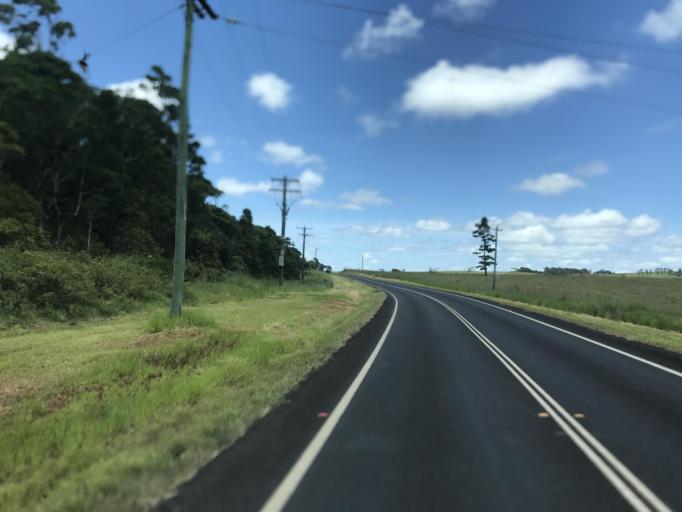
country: AU
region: Queensland
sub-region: Tablelands
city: Ravenshoe
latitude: -17.4963
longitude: 145.4768
